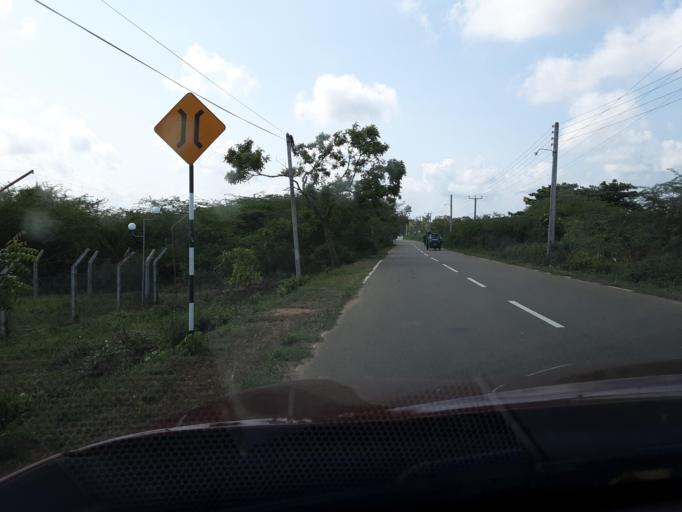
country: LK
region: Southern
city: Tangalla
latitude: 6.2096
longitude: 81.2053
